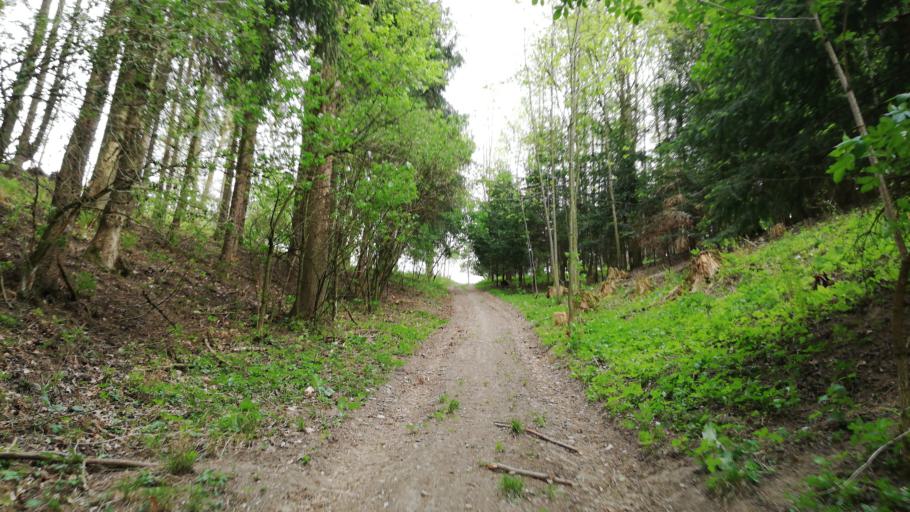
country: AT
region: Upper Austria
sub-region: Wels-Land
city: Gunskirchen
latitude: 48.1830
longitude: 13.9438
